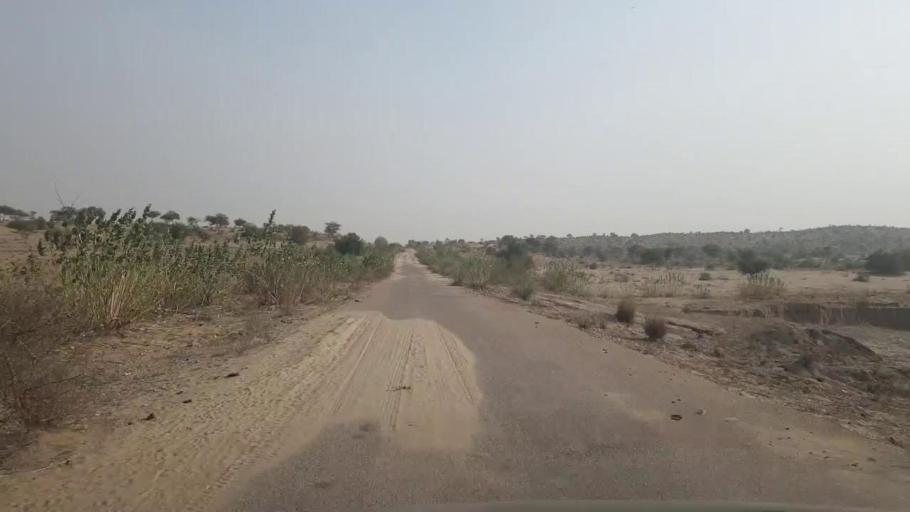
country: PK
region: Sindh
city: Chor
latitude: 25.5157
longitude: 69.9652
